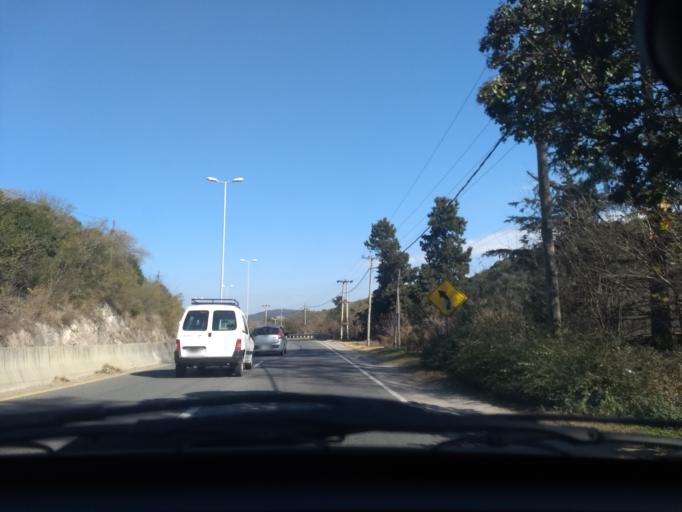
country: AR
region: Cordoba
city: Rio Ceballos
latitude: -31.1685
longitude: -64.3025
